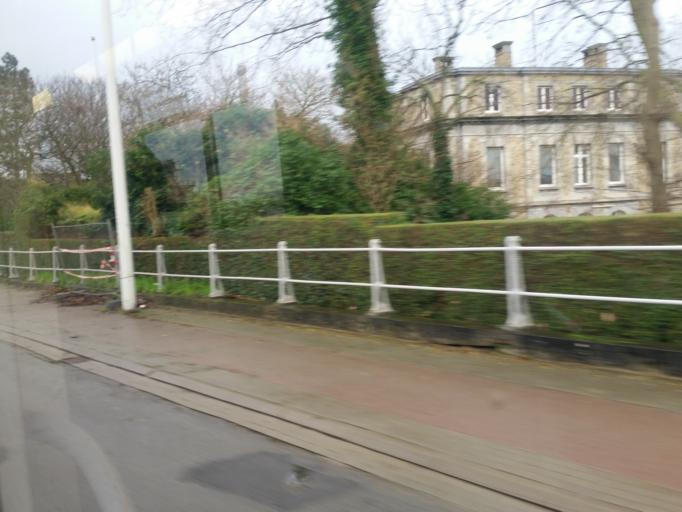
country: BE
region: Flanders
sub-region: Provincie West-Vlaanderen
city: Ostend
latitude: 51.2257
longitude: 2.9320
